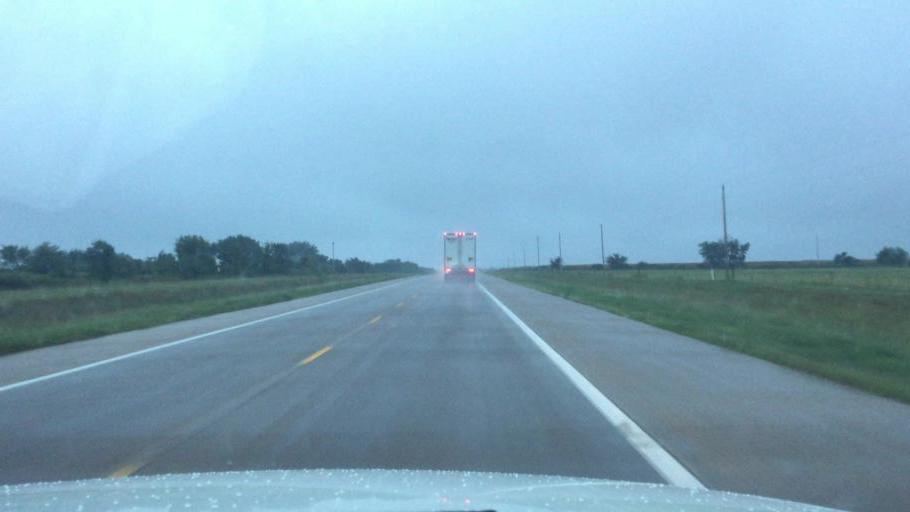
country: US
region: Kansas
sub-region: Neosho County
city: Chanute
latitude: 37.5172
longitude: -95.4708
